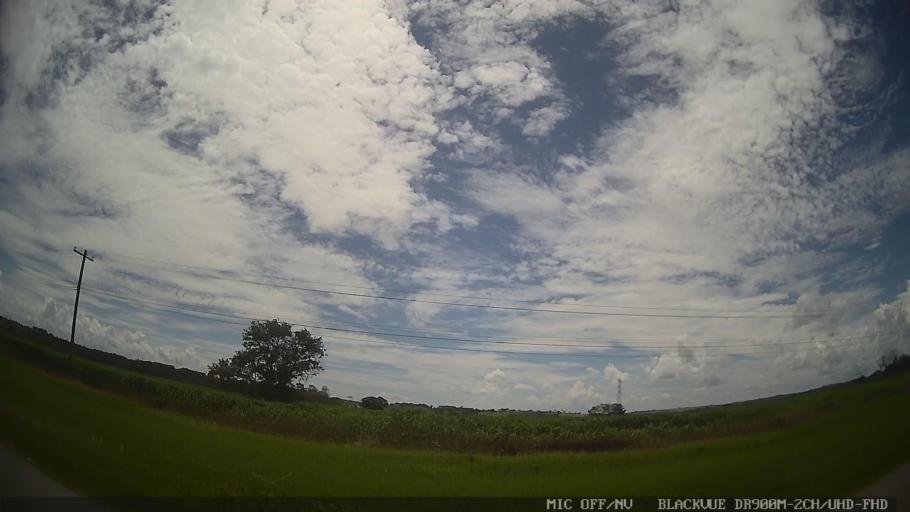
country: BR
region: Sao Paulo
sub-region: Conchas
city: Conchas
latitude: -23.0634
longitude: -47.9703
